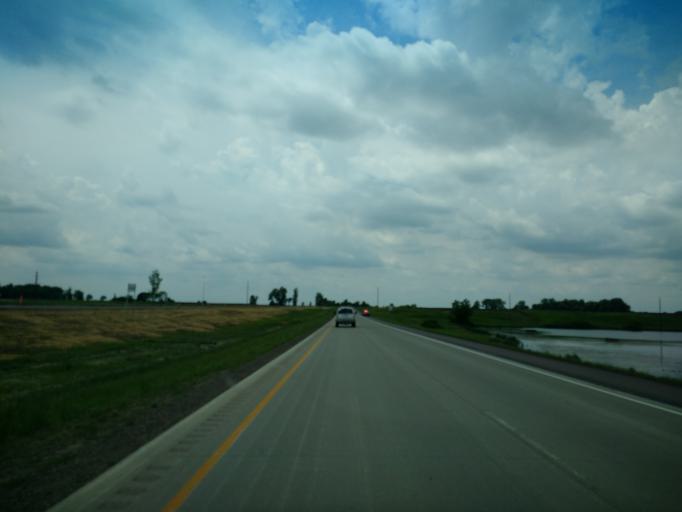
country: US
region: Minnesota
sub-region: Cottonwood County
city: Windom
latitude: 43.9060
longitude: -95.0581
